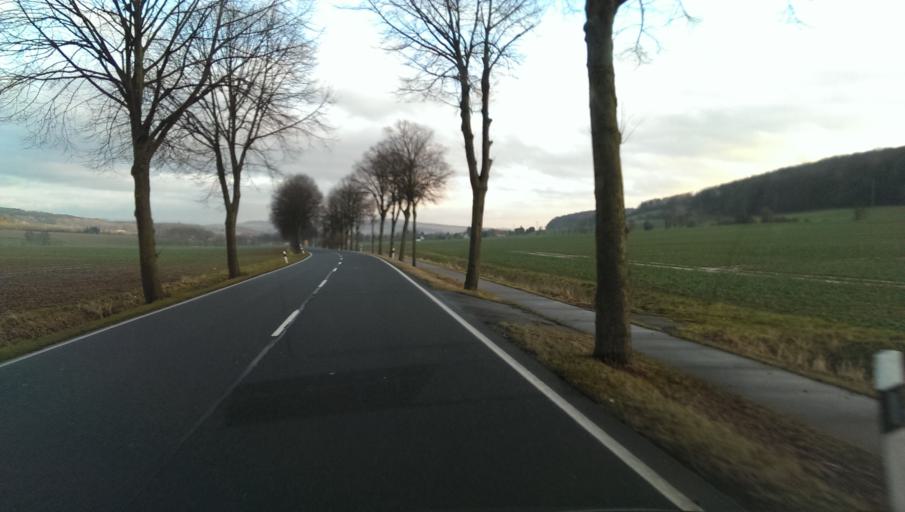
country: DE
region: Lower Saxony
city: Eimen
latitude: 51.8826
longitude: 9.7635
